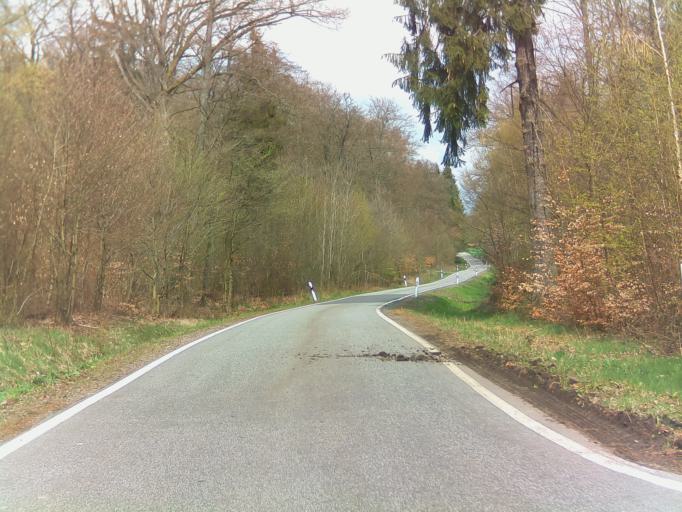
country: DE
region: Rheinland-Pfalz
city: Weitersbach
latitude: 49.8619
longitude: 7.3053
